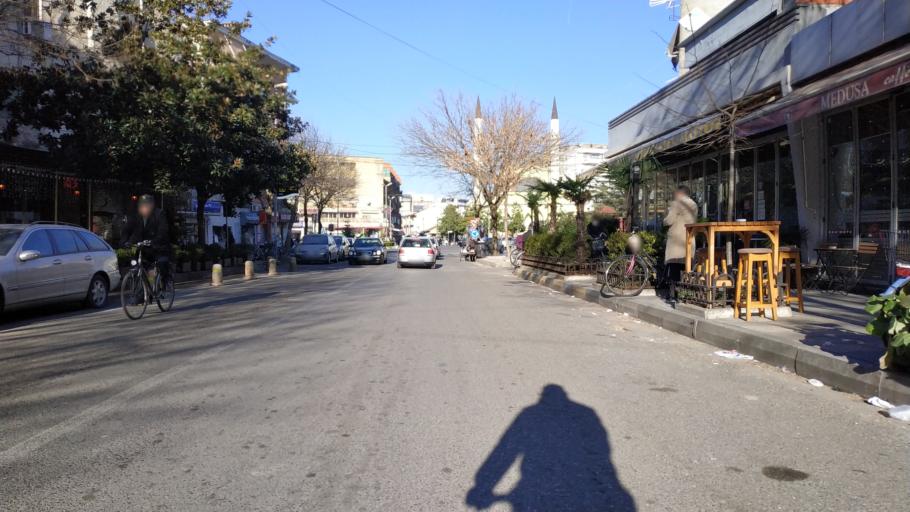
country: AL
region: Shkoder
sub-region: Rrethi i Shkodres
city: Shkoder
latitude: 42.0642
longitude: 19.5096
